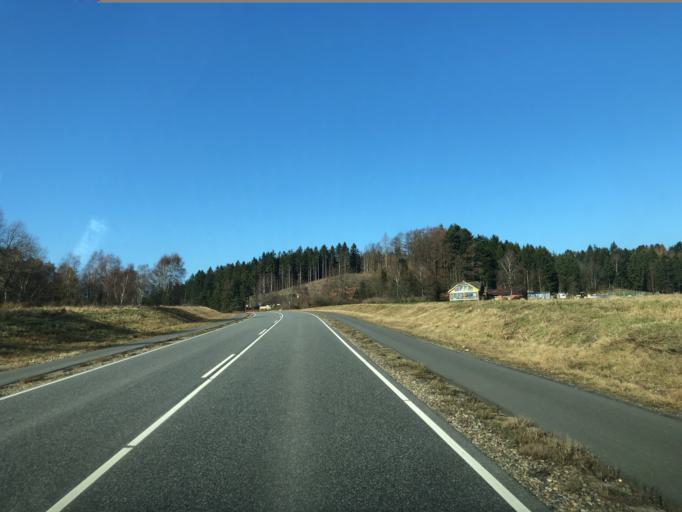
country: DK
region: Central Jutland
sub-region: Silkeborg Kommune
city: Svejbaek
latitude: 56.1861
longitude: 9.6339
